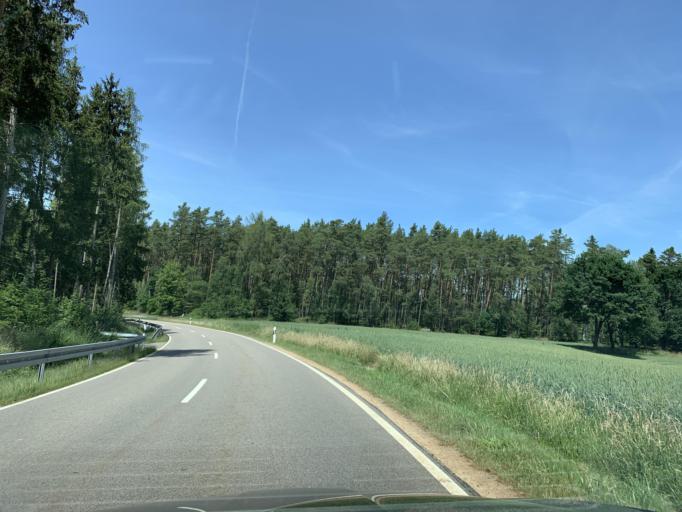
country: DE
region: Bavaria
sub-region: Upper Palatinate
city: Schwarzhofen
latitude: 49.3698
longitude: 12.3303
